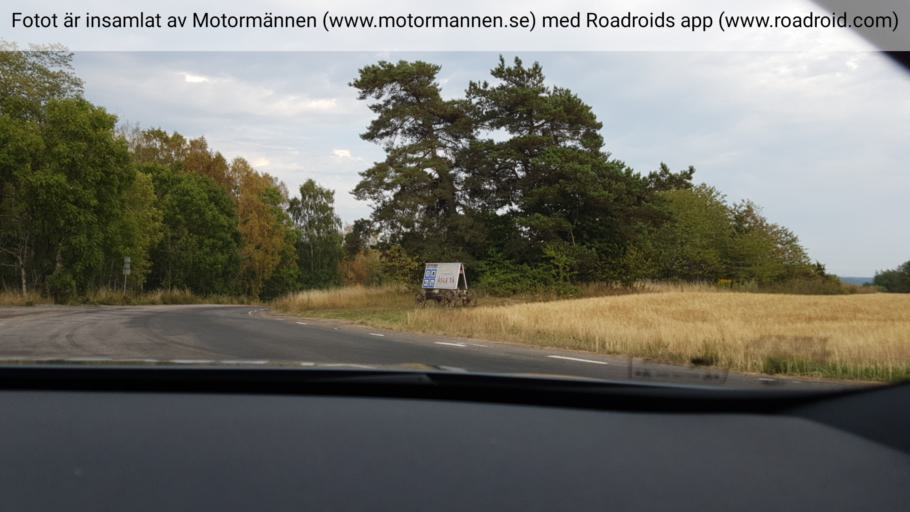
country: SE
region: Vaestra Goetaland
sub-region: Falkopings Kommun
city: Akarp
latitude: 58.1782
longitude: 13.6354
